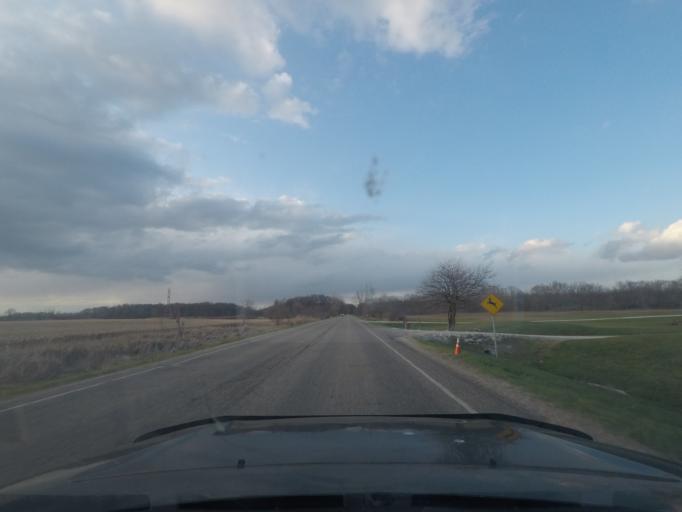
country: US
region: Indiana
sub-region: LaPorte County
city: LaPorte
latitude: 41.5480
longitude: -86.7399
